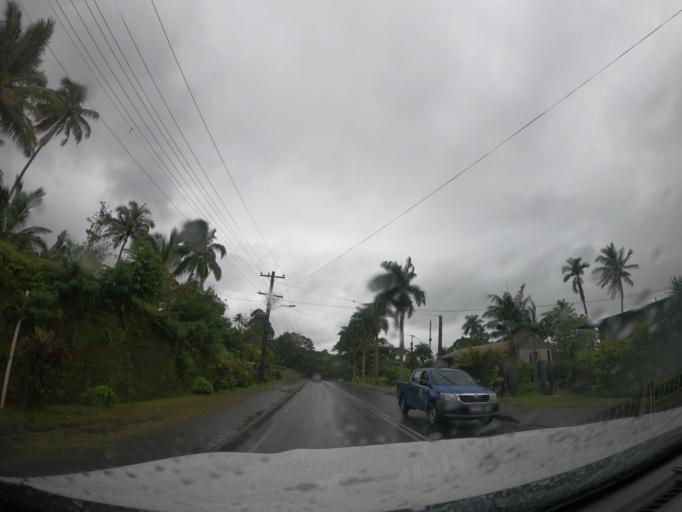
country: FJ
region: Central
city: Suva
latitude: -18.1132
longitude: 178.4211
